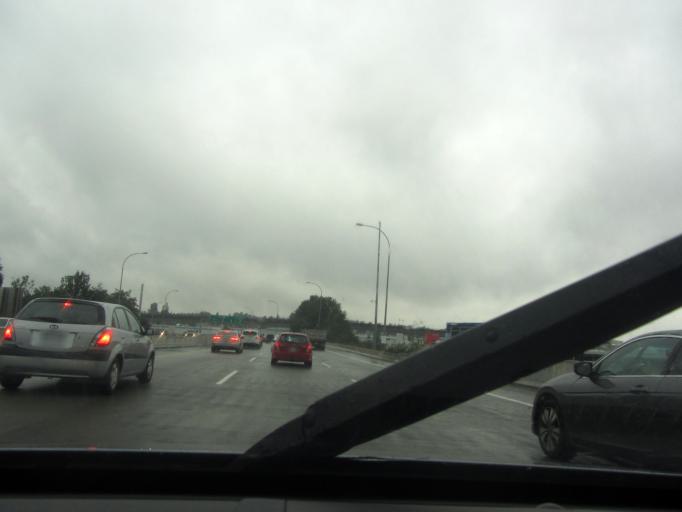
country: CA
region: British Columbia
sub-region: Fraser Valley Regional District
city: North Vancouver
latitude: 49.2648
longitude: -123.0261
